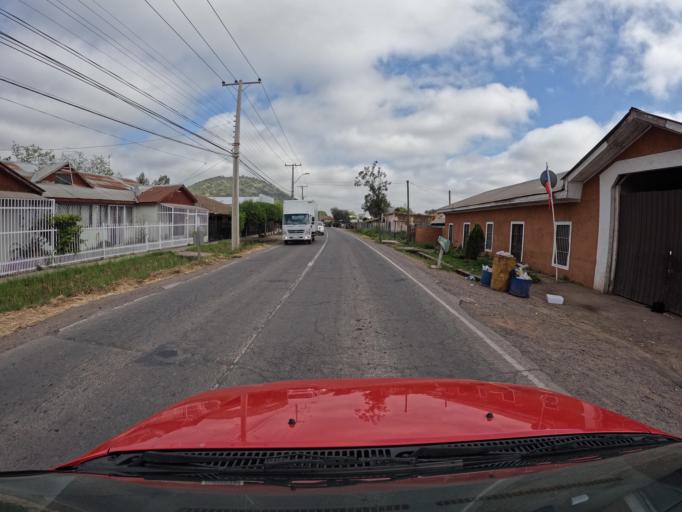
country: CL
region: O'Higgins
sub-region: Provincia de Colchagua
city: Santa Cruz
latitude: -34.7086
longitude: -71.2954
